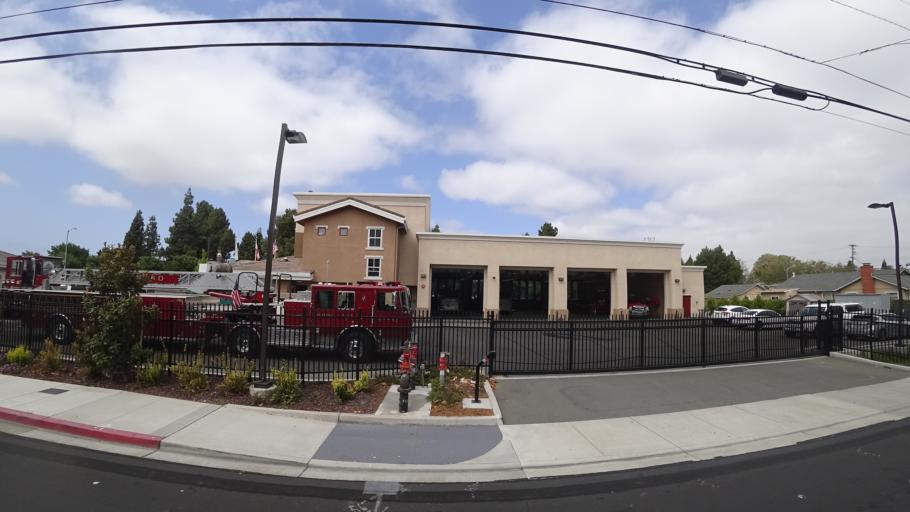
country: US
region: California
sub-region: Alameda County
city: Hayward
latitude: 37.6328
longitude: -122.0635
